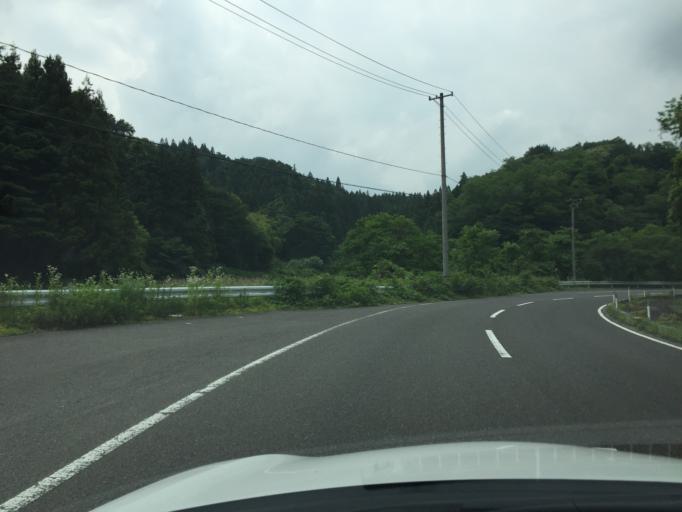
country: JP
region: Fukushima
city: Funehikimachi-funehiki
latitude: 37.2883
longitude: 140.5909
